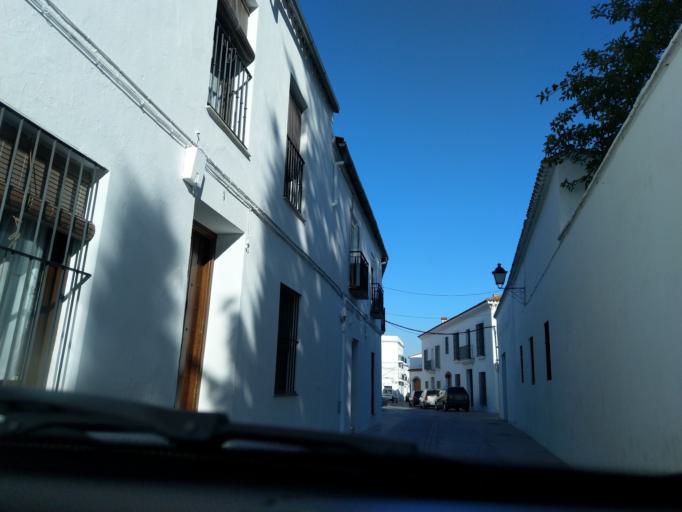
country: ES
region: Extremadura
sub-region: Provincia de Badajoz
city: Llerena
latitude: 38.2392
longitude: -6.0154
